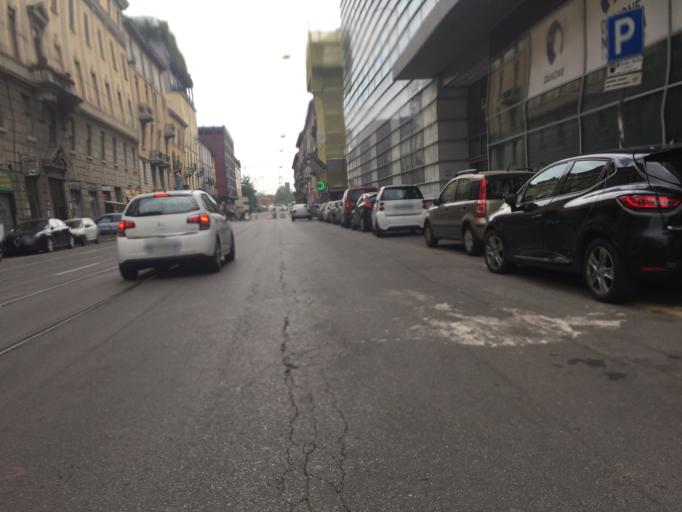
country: IT
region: Lombardy
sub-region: Citta metropolitana di Milano
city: Milano
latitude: 45.4907
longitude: 9.1836
